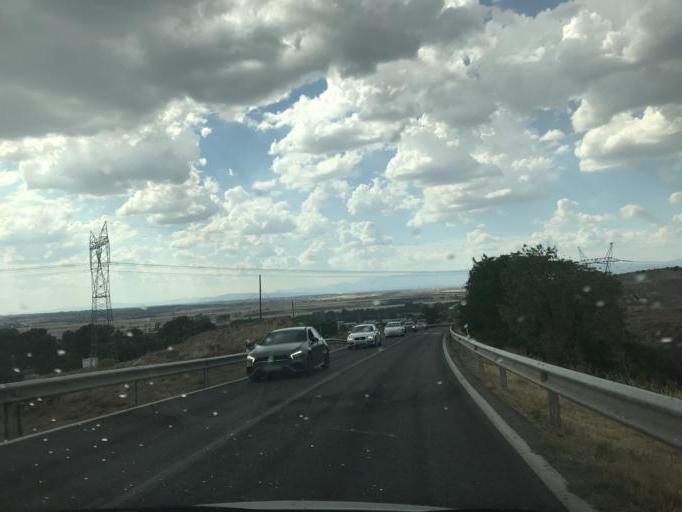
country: ES
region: Madrid
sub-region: Provincia de Madrid
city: Paracuellos de Jarama
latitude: 40.5060
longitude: -3.5359
